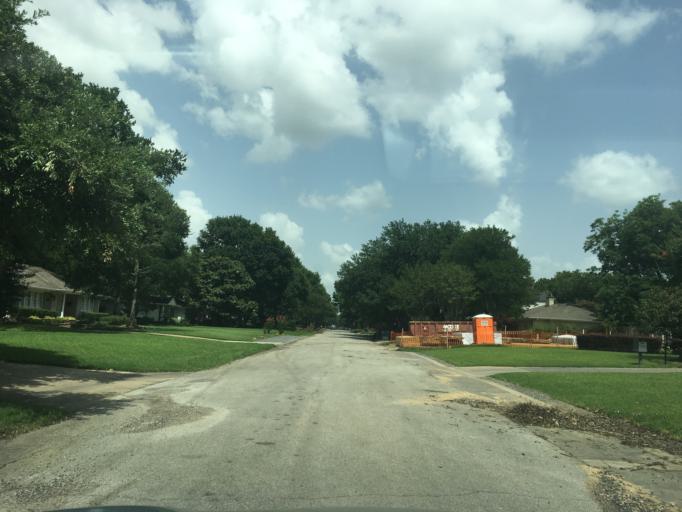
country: US
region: Texas
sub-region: Dallas County
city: University Park
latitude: 32.8894
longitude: -96.7955
